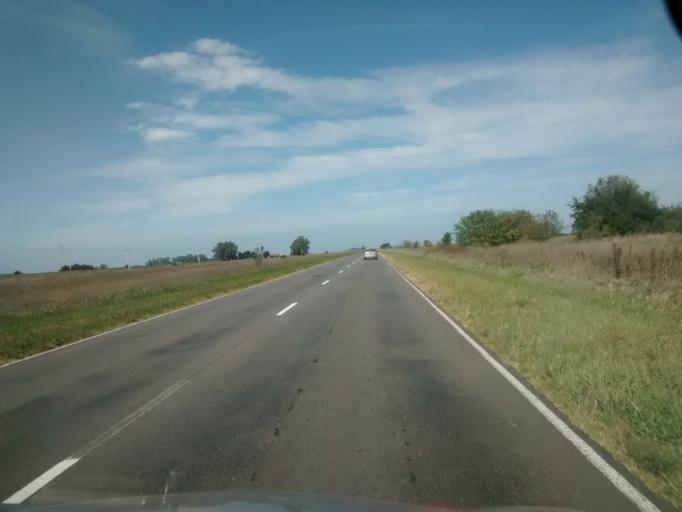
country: AR
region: Buenos Aires
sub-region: Partido de Ayacucho
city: Ayacucho
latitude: -36.6554
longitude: -58.5740
